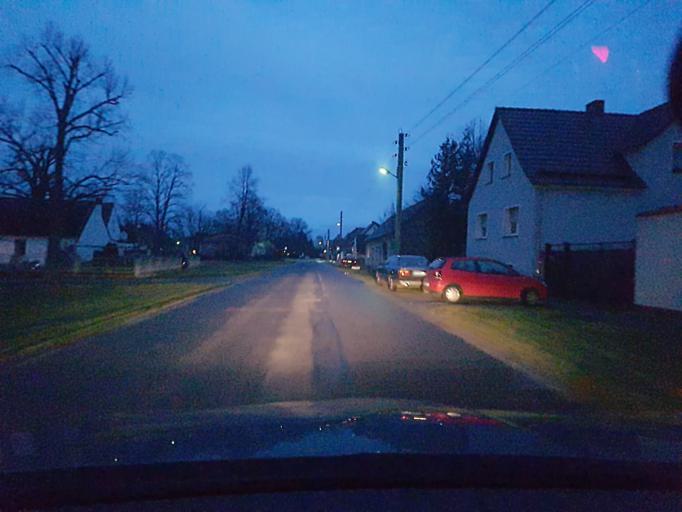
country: DE
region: Brandenburg
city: Ruckersdorf
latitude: 51.5914
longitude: 13.5390
